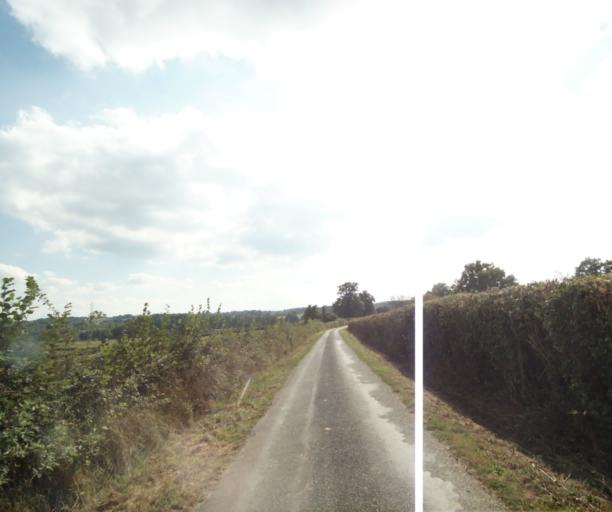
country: FR
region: Bourgogne
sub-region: Departement de Saone-et-Loire
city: Palinges
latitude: 46.4967
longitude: 4.2352
